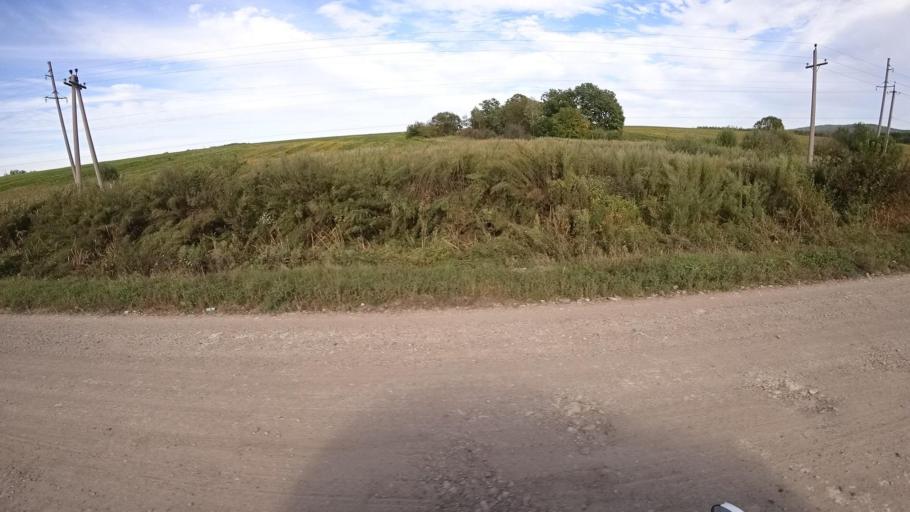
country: RU
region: Primorskiy
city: Dostoyevka
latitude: 44.3101
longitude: 133.4642
